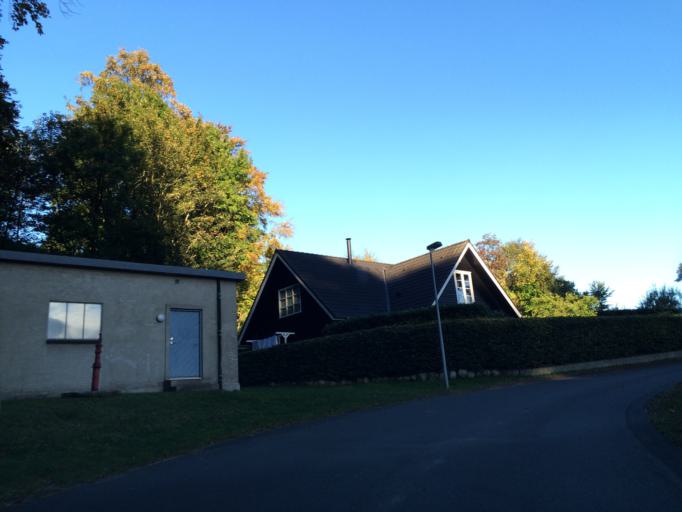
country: DK
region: Central Jutland
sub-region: Skanderborg Kommune
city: Ry
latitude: 56.1272
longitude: 9.7189
